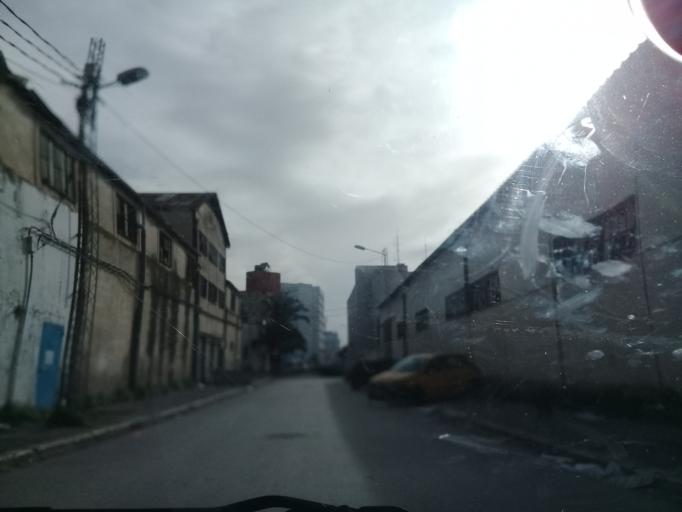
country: TN
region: Tunis
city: Tunis
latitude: 36.7942
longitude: 10.1889
